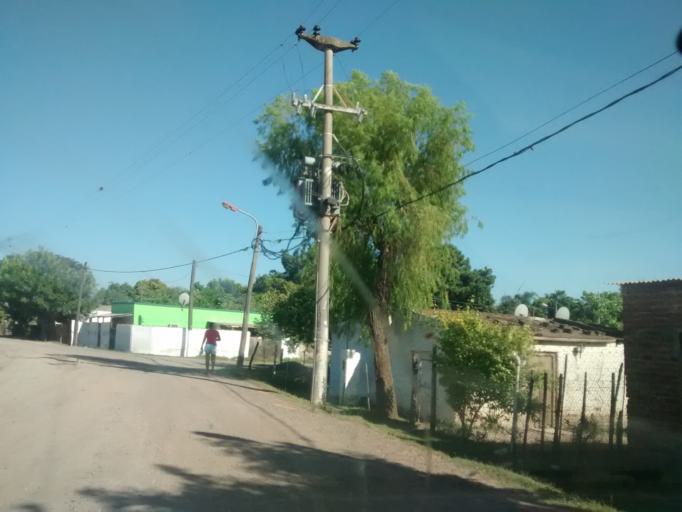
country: AR
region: Chaco
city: Resistencia
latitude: -27.4259
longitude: -58.9809
